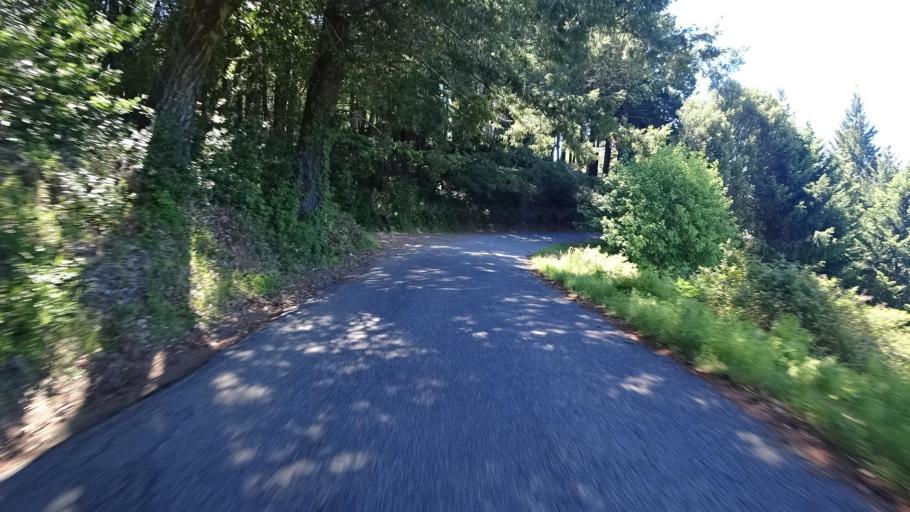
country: US
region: California
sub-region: Humboldt County
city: Redway
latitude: 40.1183
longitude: -123.9687
